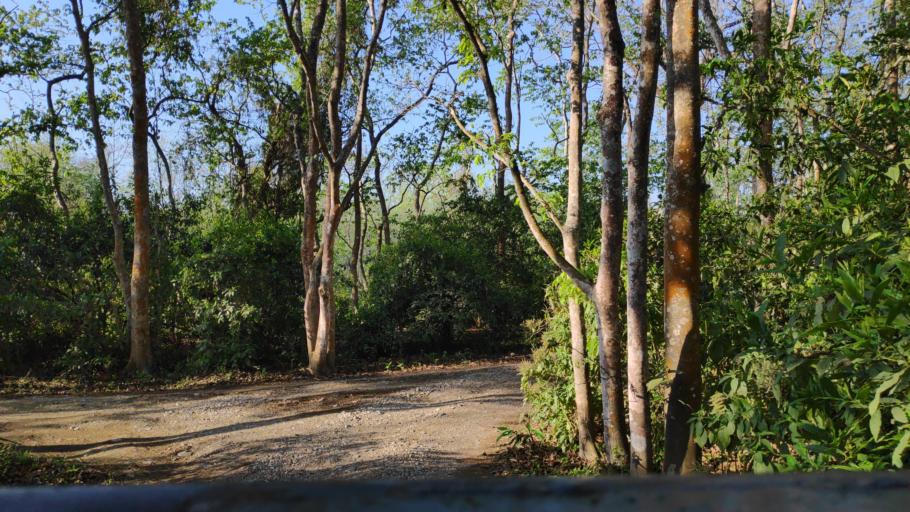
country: NP
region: Central Region
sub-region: Narayani Zone
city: Bharatpur
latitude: 27.5593
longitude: 84.5633
